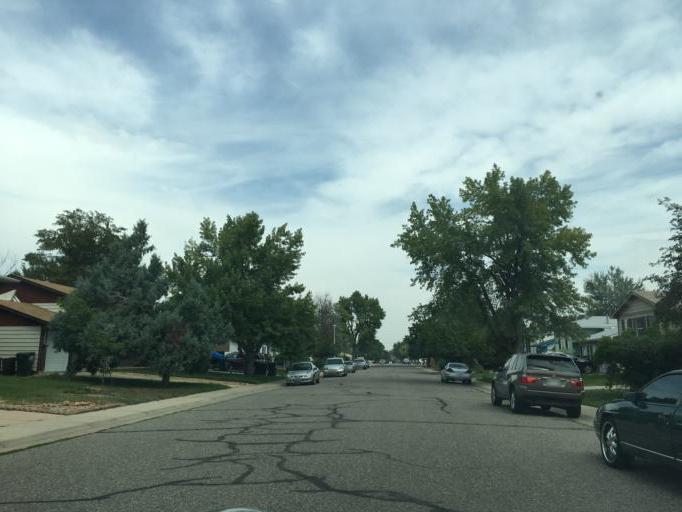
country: US
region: Colorado
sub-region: Adams County
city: Aurora
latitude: 39.7323
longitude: -104.7971
